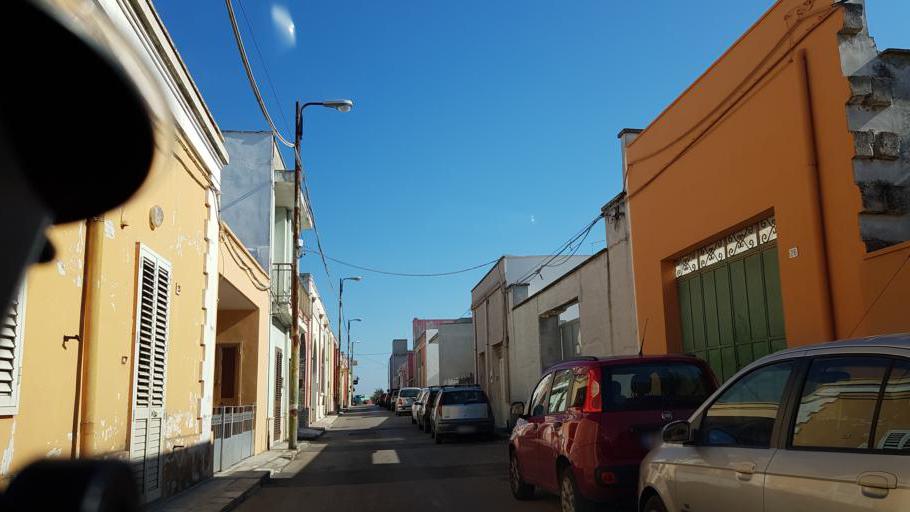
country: IT
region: Apulia
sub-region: Provincia di Brindisi
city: Torchiarolo
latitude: 40.4840
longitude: 18.0555
